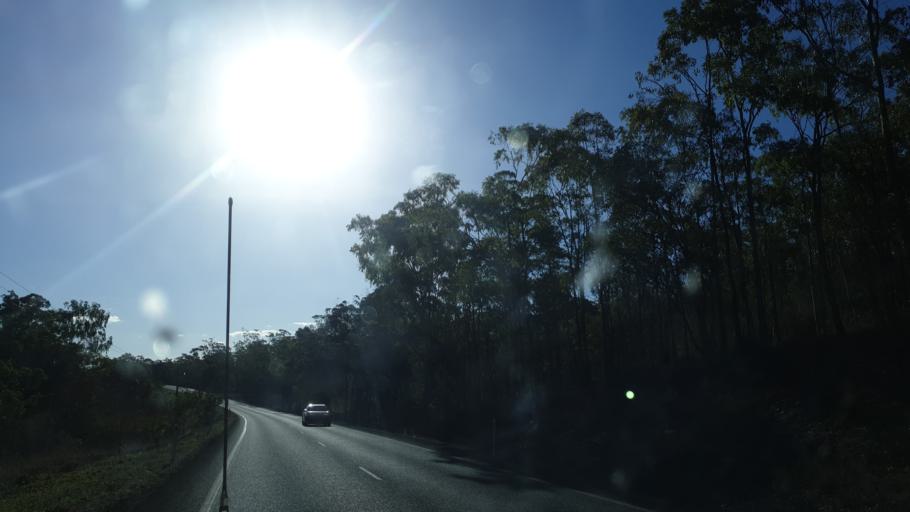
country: AU
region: Queensland
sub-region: Tablelands
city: Atherton
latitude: -17.3637
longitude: 145.4003
